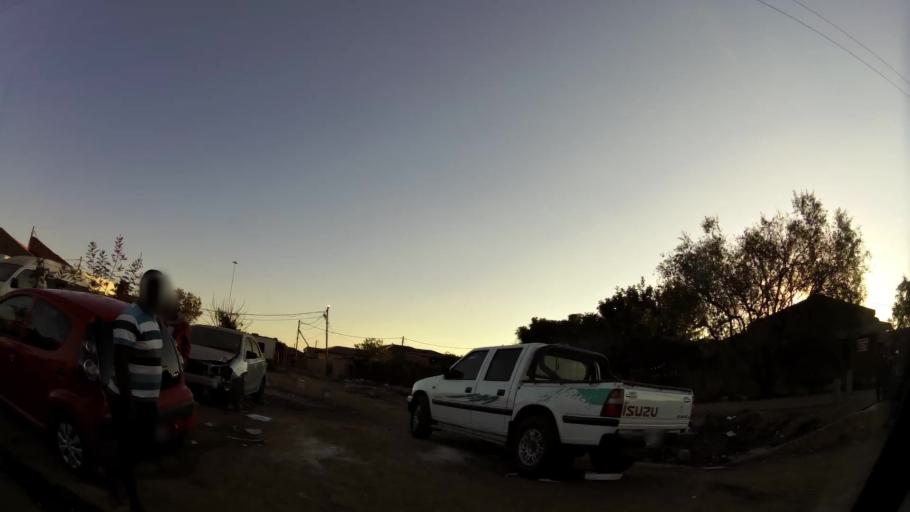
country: ZA
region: Gauteng
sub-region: City of Tshwane Metropolitan Municipality
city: Cullinan
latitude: -25.7185
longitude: 28.3959
